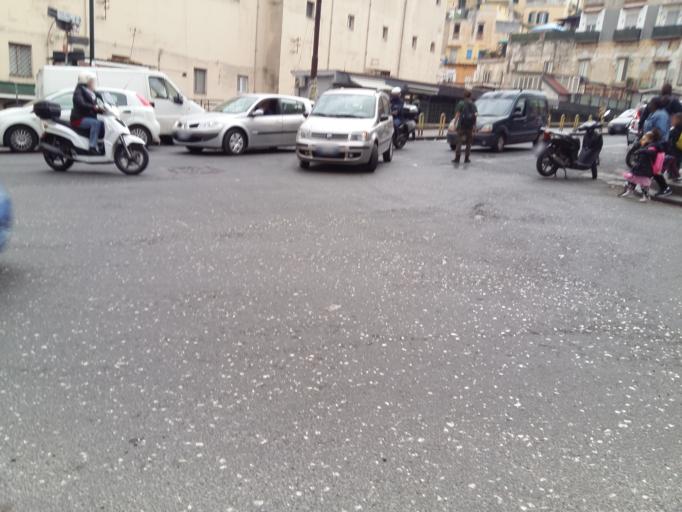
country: IT
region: Campania
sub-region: Provincia di Napoli
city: Napoli
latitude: 40.8530
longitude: 14.2453
